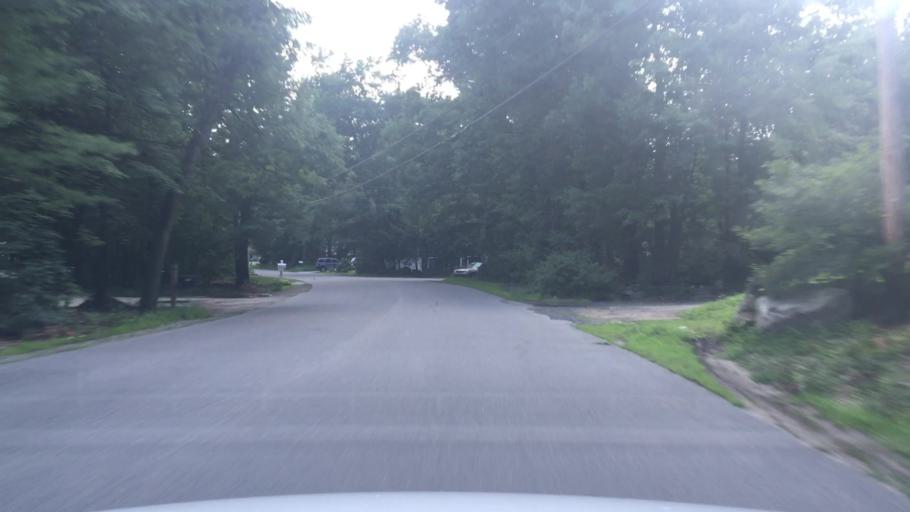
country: US
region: New Hampshire
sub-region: Rockingham County
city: Derry Village
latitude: 42.9206
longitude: -71.3263
